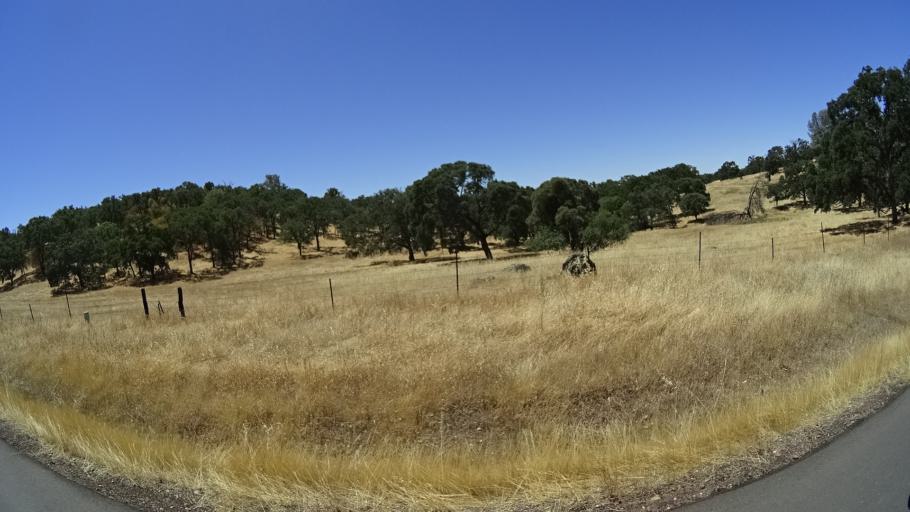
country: US
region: California
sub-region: Calaveras County
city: Rancho Calaveras
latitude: 38.0504
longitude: -120.7936
